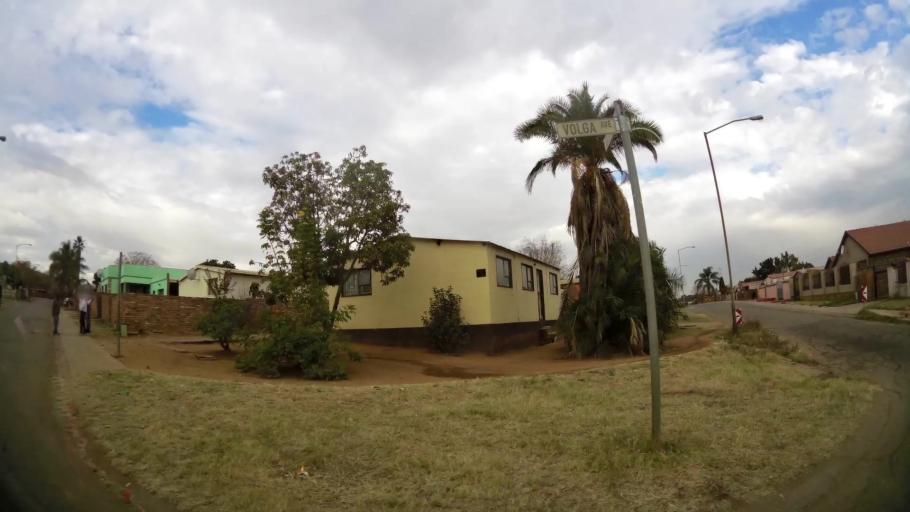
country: ZA
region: Gauteng
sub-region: City of Tshwane Metropolitan Municipality
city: Pretoria
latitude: -25.6994
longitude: 28.2986
